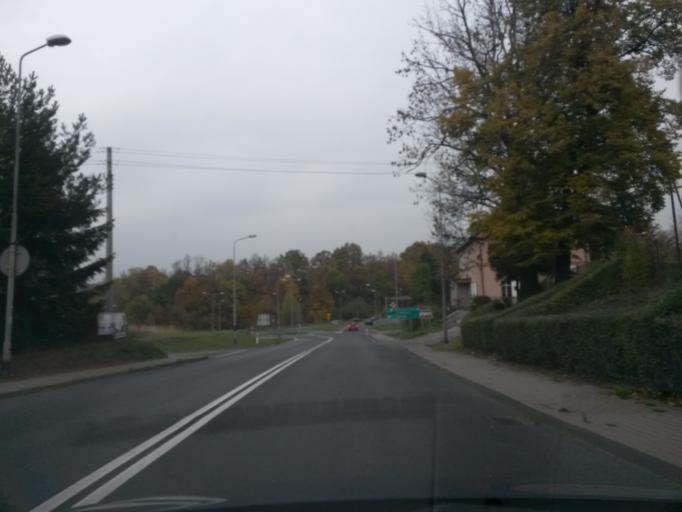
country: PL
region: Lower Silesian Voivodeship
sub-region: Powiat klodzki
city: Klodzko
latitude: 50.4568
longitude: 16.6707
